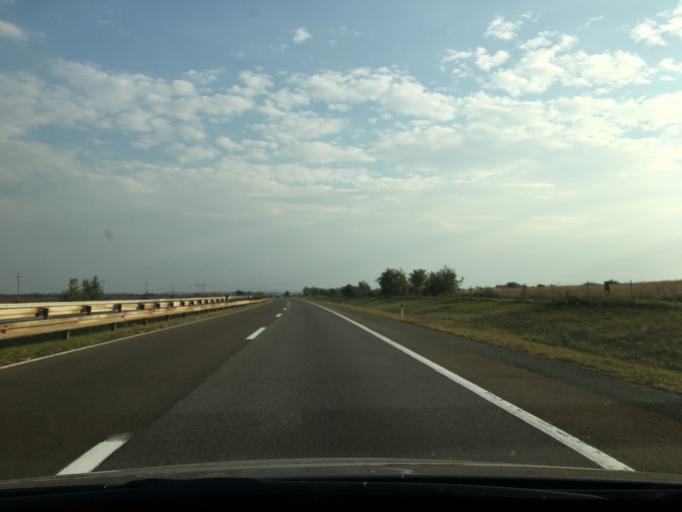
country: RS
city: Lugavcina
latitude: 44.5647
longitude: 20.9810
